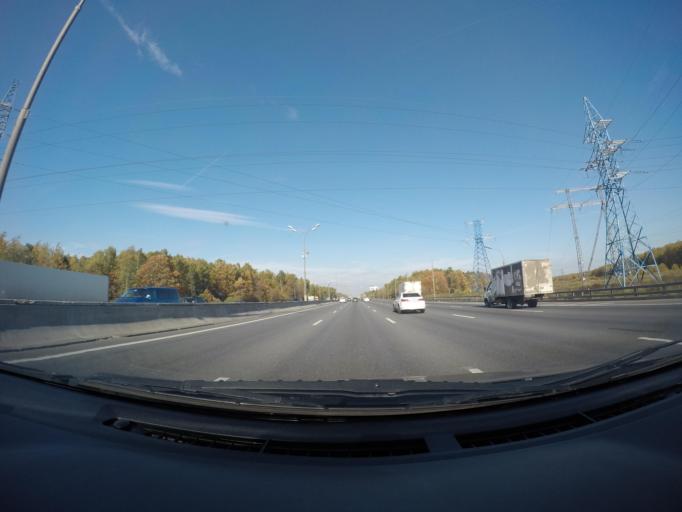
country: RU
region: Moscow
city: Ivanovskoye
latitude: 55.7878
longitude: 37.8417
